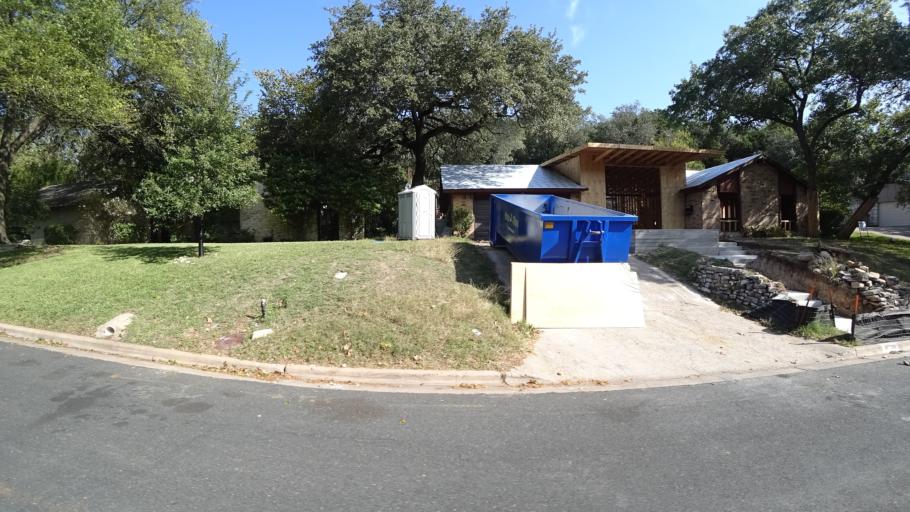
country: US
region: Texas
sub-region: Travis County
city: West Lake Hills
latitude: 30.3533
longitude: -97.7634
